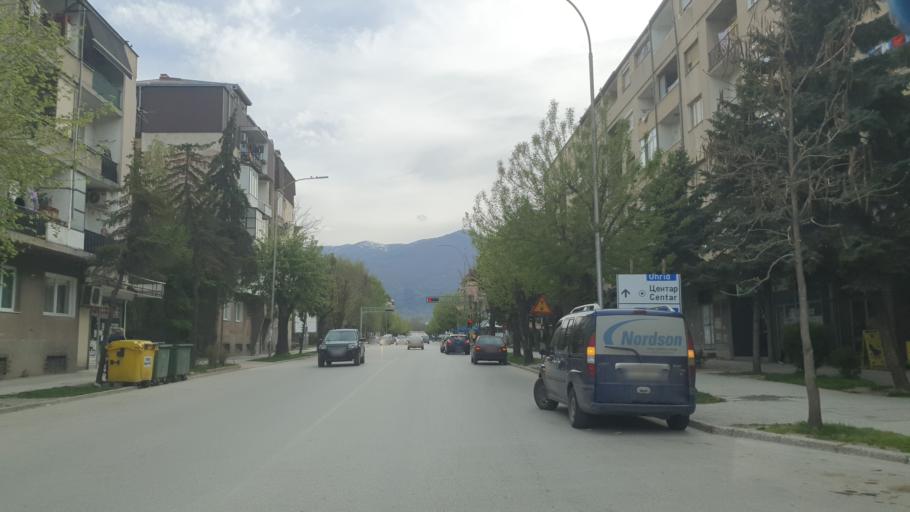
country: MK
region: Bitola
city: Bitola
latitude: 41.0357
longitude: 21.3407
